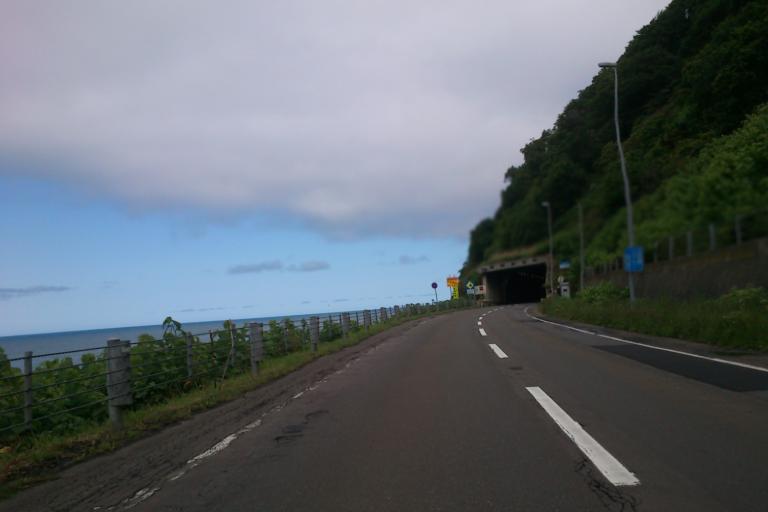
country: JP
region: Hokkaido
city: Ishikari
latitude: 43.4370
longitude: 141.4171
